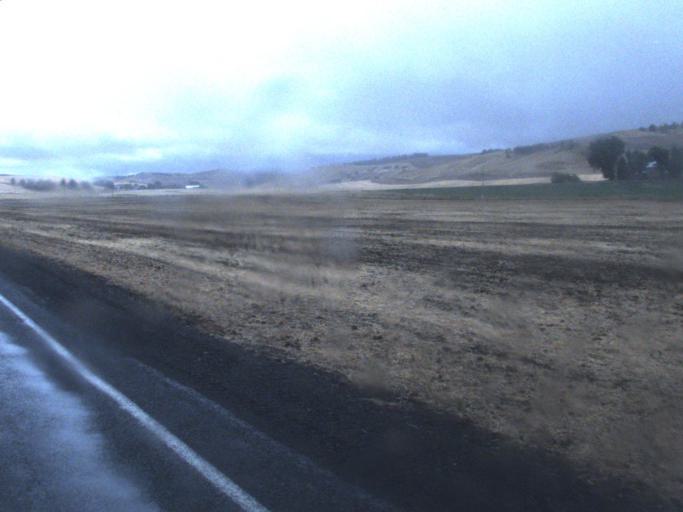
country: US
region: Washington
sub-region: Whitman County
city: Colfax
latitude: 47.0683
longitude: -117.5305
